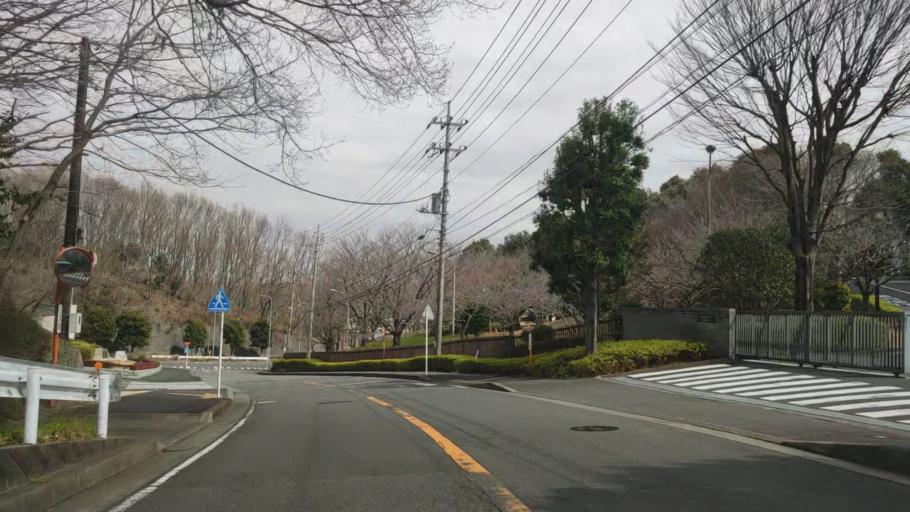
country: JP
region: Kanagawa
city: Hadano
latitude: 35.3375
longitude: 139.2278
